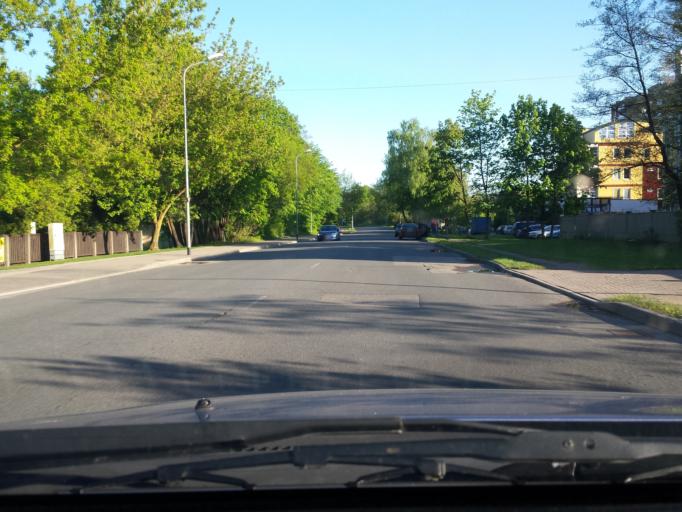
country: LV
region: Riga
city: Jaunciems
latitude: 56.9973
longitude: 24.1713
